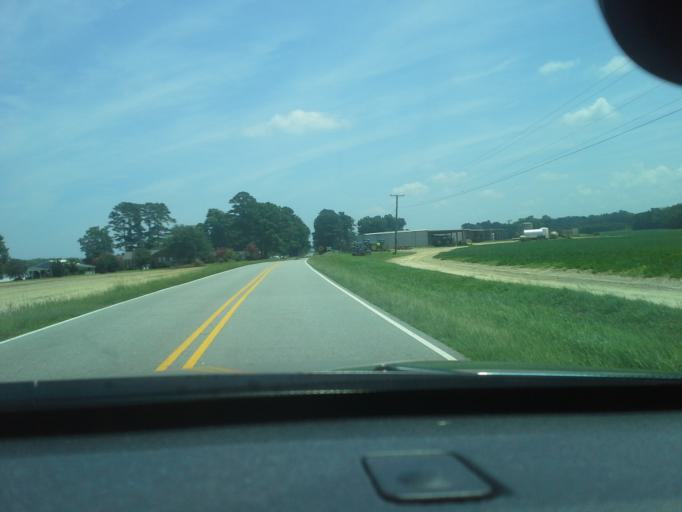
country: US
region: North Carolina
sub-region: Washington County
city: Plymouth
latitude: 35.9208
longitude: -76.6410
